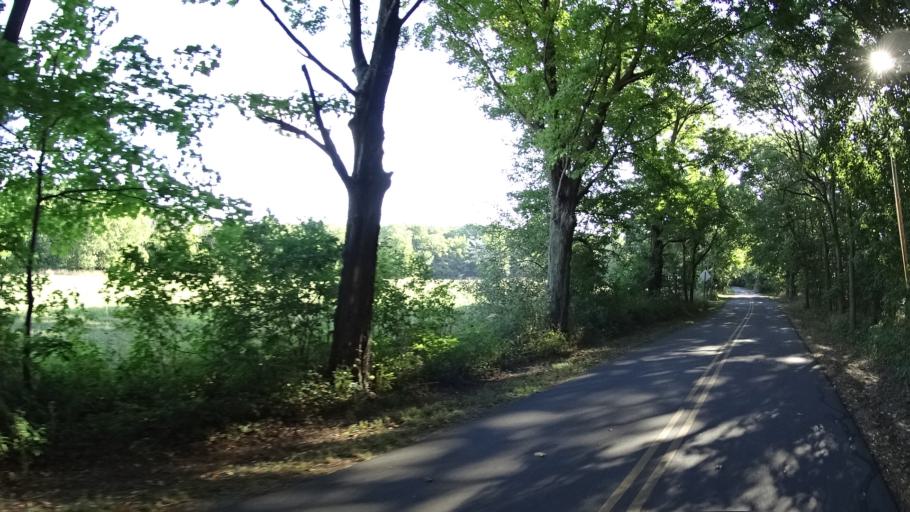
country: US
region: Ohio
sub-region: Erie County
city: Sandusky
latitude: 41.6128
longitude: -82.7218
